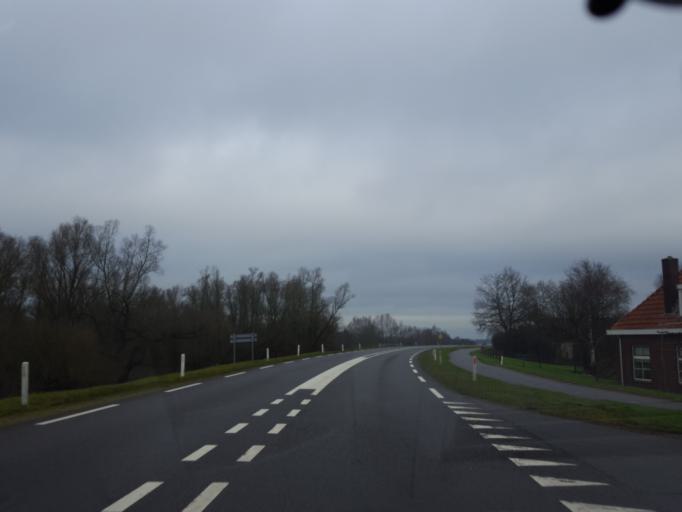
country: NL
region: Overijssel
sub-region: Gemeente Olst-Wijhe
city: Boskamp
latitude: 52.2978
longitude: 6.1130
